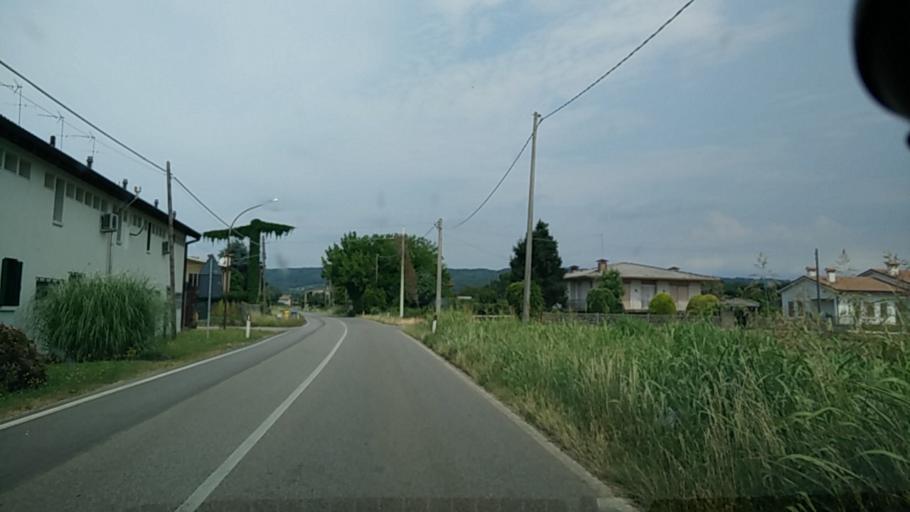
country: IT
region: Veneto
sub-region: Provincia di Treviso
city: Selva del Montello
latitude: 45.7696
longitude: 12.1481
